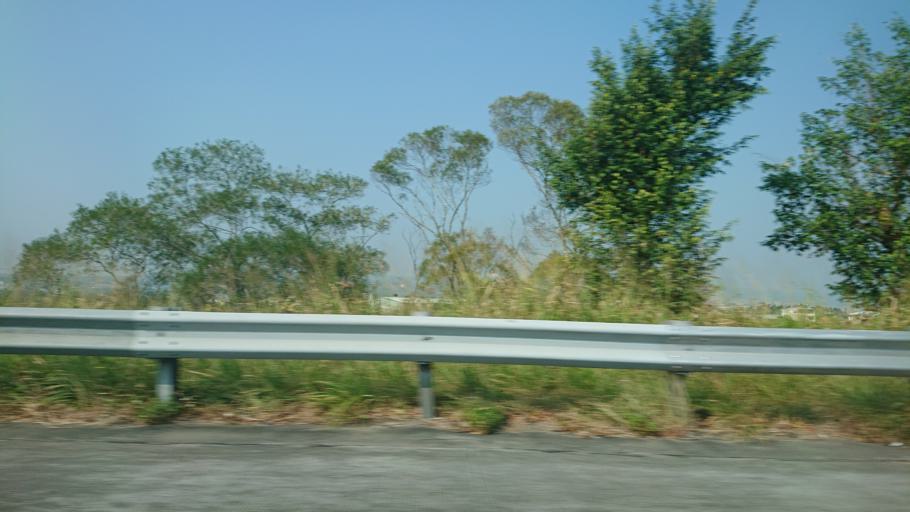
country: TW
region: Taiwan
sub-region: Nantou
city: Nantou
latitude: 23.8896
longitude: 120.7101
